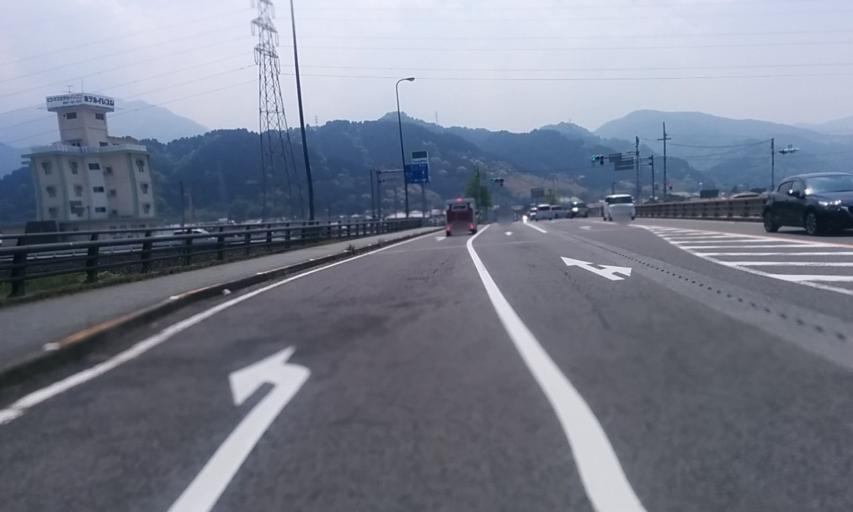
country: JP
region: Ehime
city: Saijo
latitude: 33.9029
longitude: 133.1839
